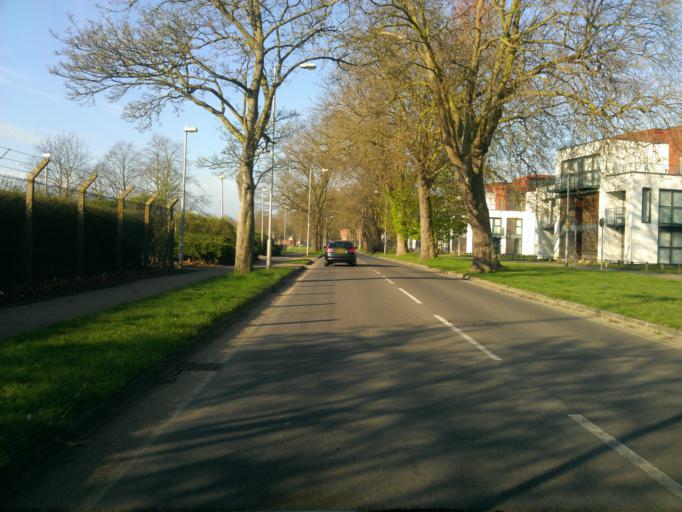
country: GB
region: England
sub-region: Essex
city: Colchester
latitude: 51.8821
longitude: 0.8949
